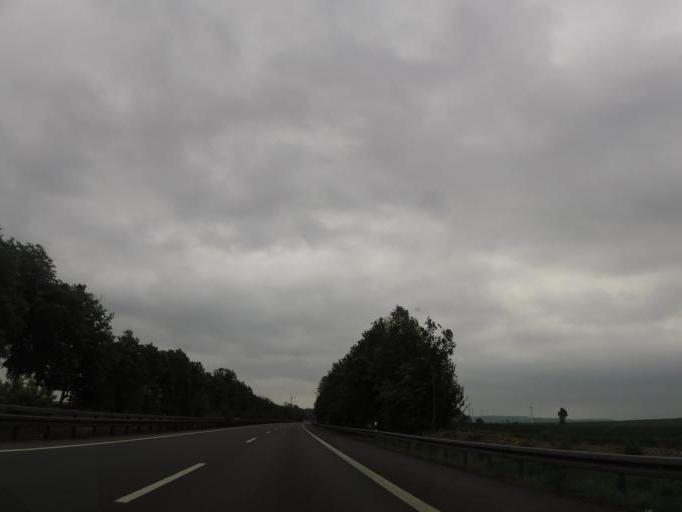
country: DE
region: Lower Saxony
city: Holle
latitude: 52.0934
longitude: 10.1692
